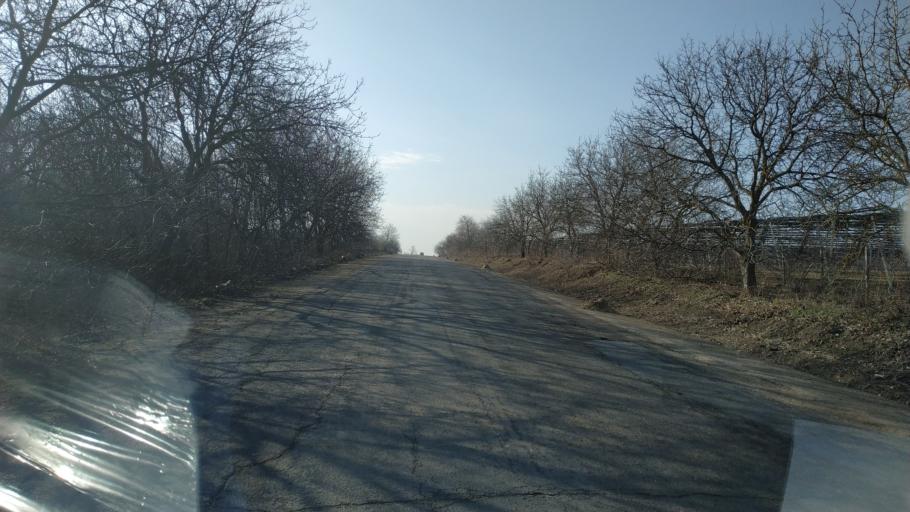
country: MD
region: Chisinau
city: Singera
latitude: 46.8614
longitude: 29.0317
